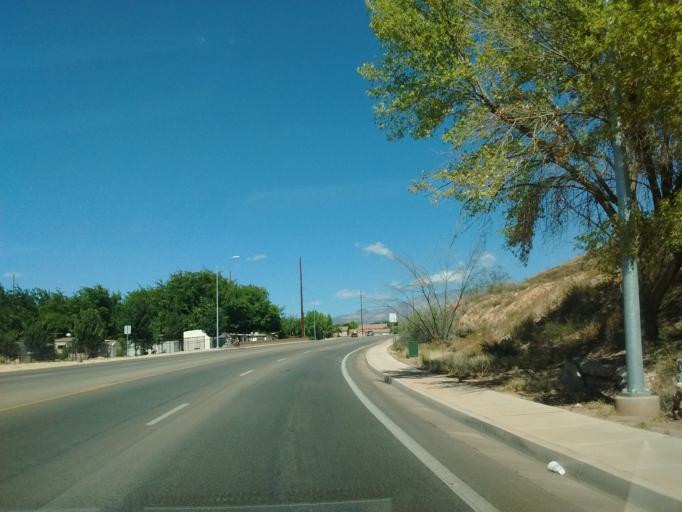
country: US
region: Utah
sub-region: Washington County
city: Washington
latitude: 37.1236
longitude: -113.5051
